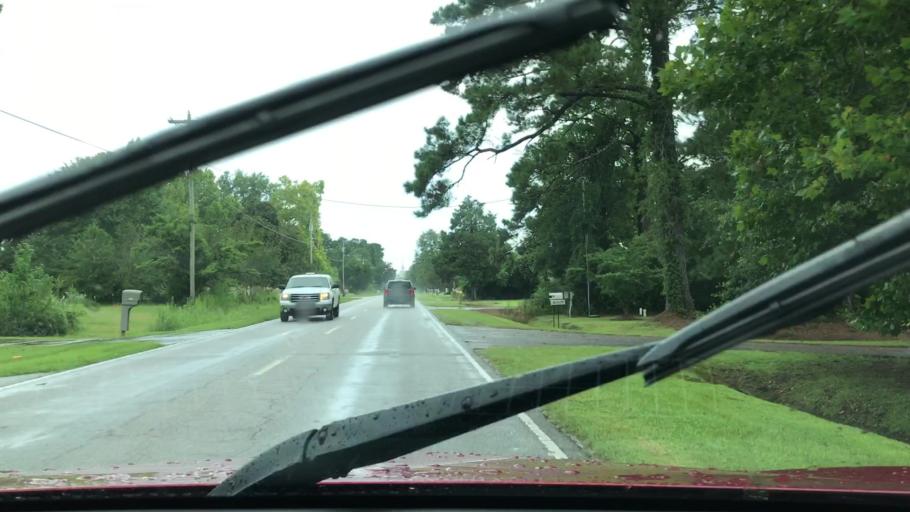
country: US
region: South Carolina
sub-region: Horry County
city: Red Hill
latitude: 33.8510
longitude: -79.0166
